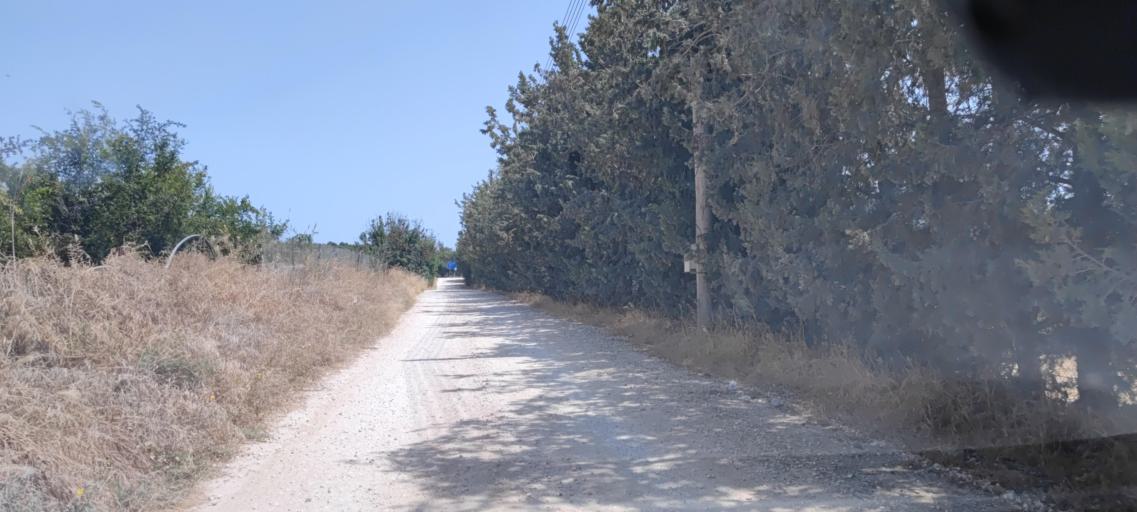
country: CY
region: Limassol
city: Pissouri
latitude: 34.7188
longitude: 32.5947
